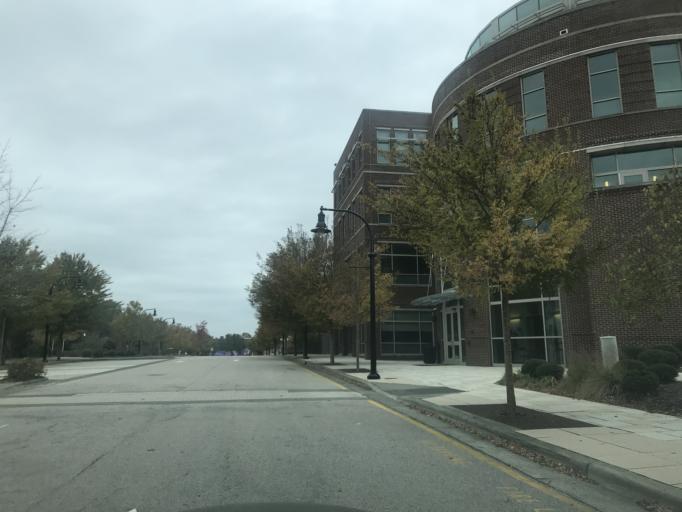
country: US
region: North Carolina
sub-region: Wake County
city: Wake Forest
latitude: 35.9768
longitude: -78.5077
